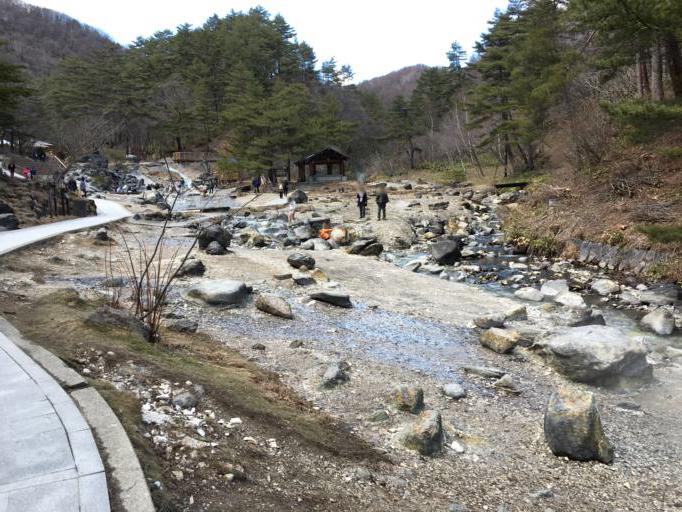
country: JP
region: Gunma
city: Nakanojomachi
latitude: 36.6241
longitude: 138.5901
